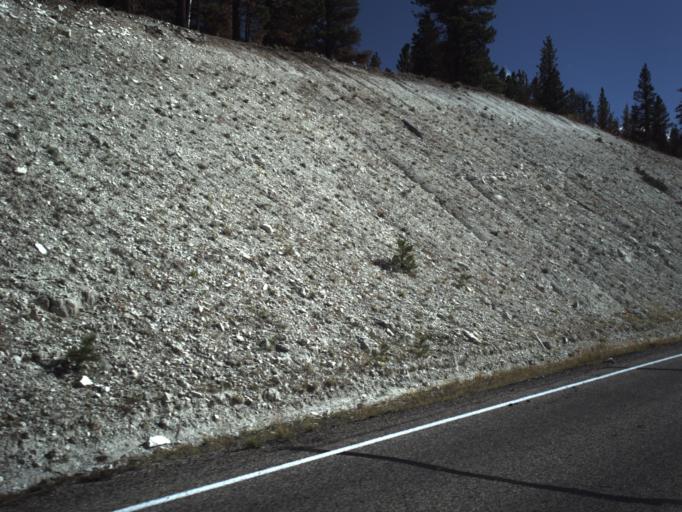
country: US
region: Utah
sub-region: Iron County
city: Parowan
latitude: 37.6927
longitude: -112.6645
